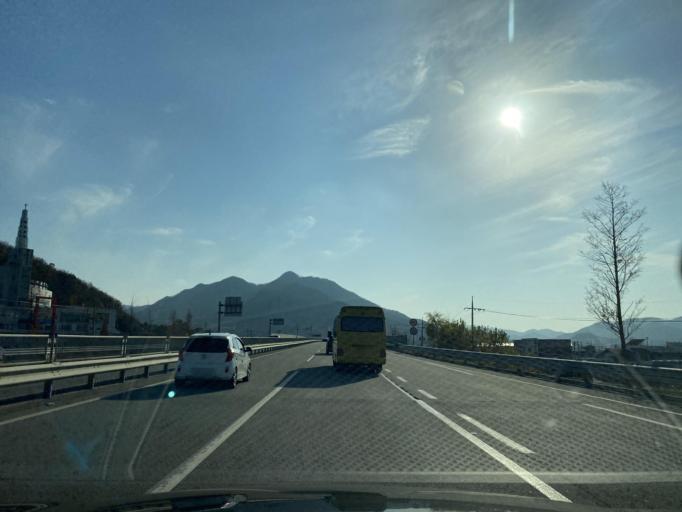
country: KR
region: Chungcheongnam-do
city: Asan
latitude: 36.7661
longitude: 127.0376
